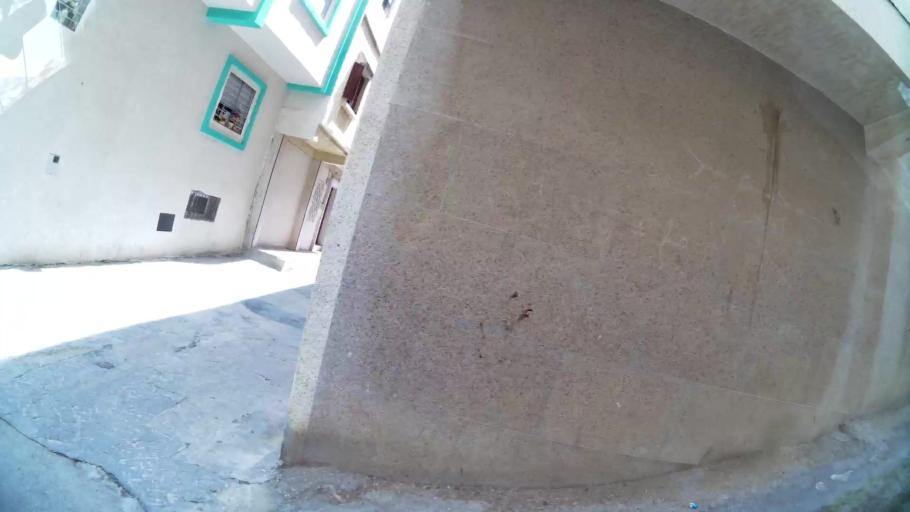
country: MA
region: Tanger-Tetouan
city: Tetouan
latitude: 35.5776
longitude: -5.3515
